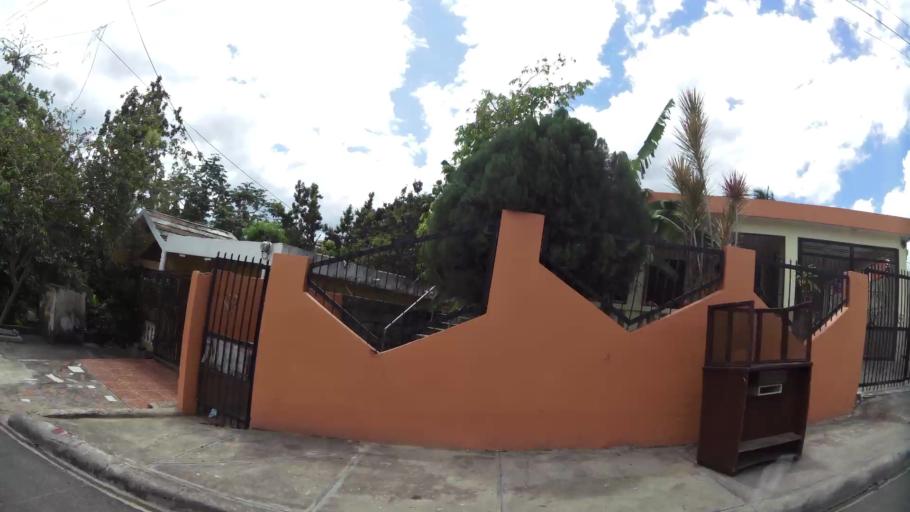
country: DO
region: Nacional
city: Ensanche Luperon
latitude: 18.5248
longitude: -69.9078
